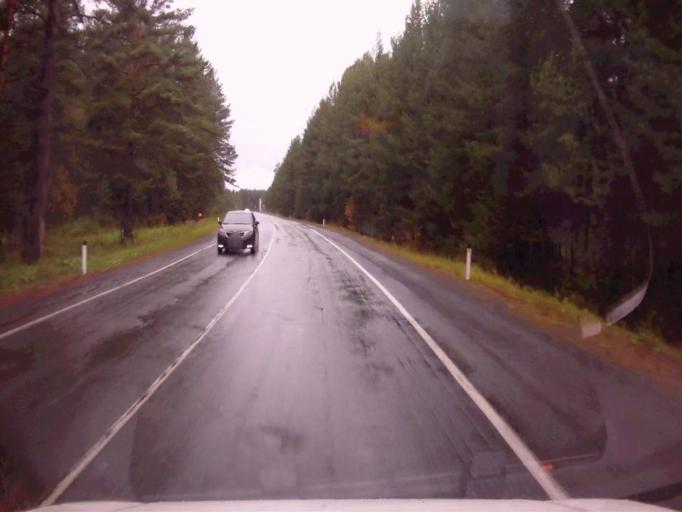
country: RU
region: Chelyabinsk
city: Verkhniy Ufaley
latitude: 56.0260
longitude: 60.2944
